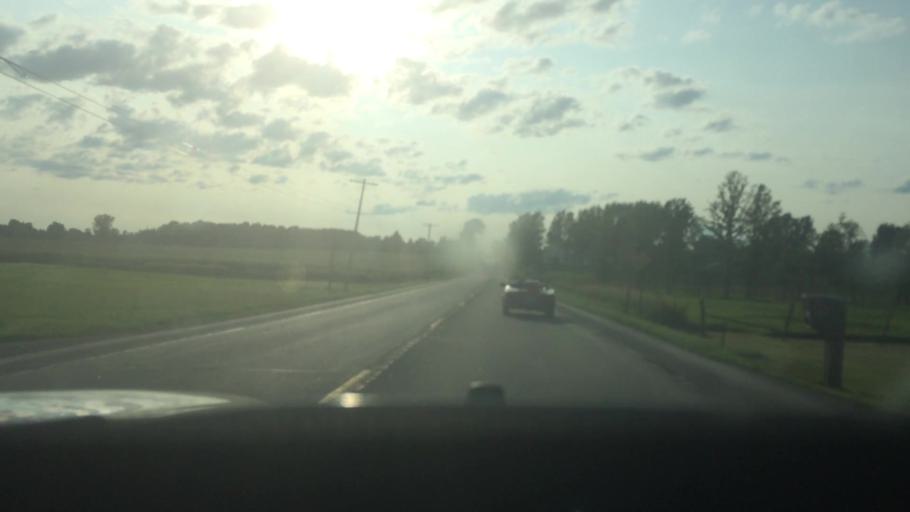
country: US
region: New York
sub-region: St. Lawrence County
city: Ogdensburg
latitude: 44.6644
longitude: -75.3493
